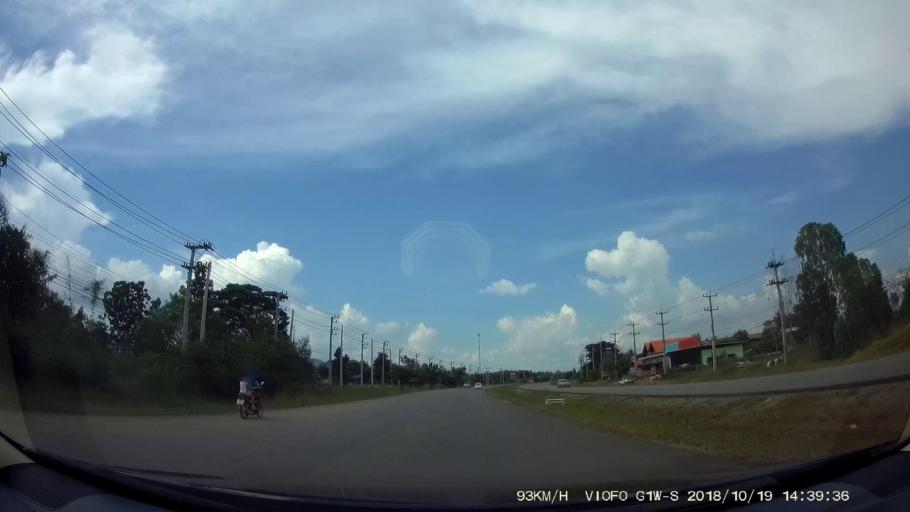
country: TH
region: Chaiyaphum
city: Kaeng Khro
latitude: 16.2281
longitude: 102.1947
